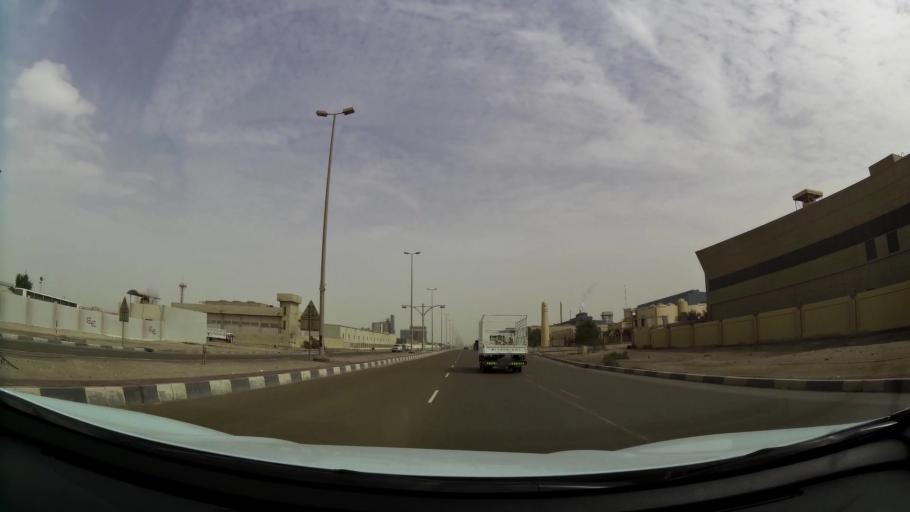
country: AE
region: Abu Dhabi
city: Abu Dhabi
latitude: 24.3222
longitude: 54.4769
